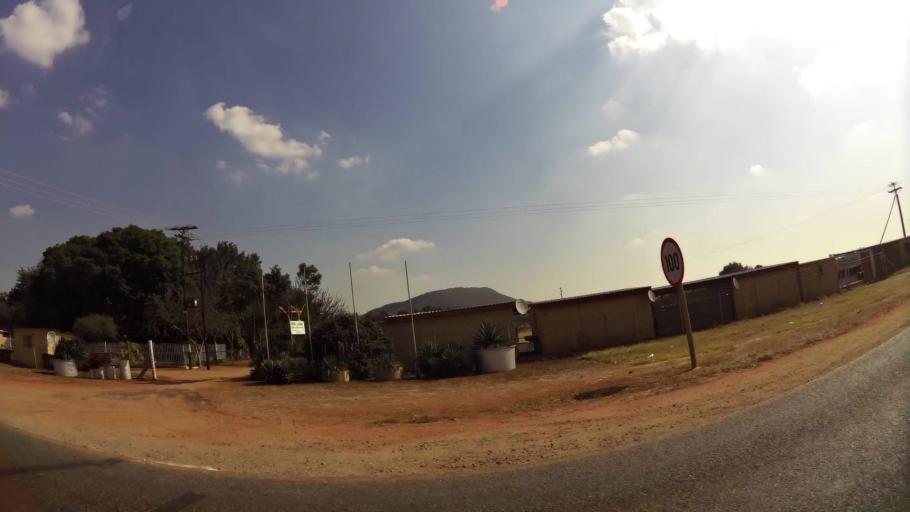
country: ZA
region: North-West
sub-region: Bojanala Platinum District Municipality
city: Rustenburg
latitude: -25.4901
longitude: 27.0858
